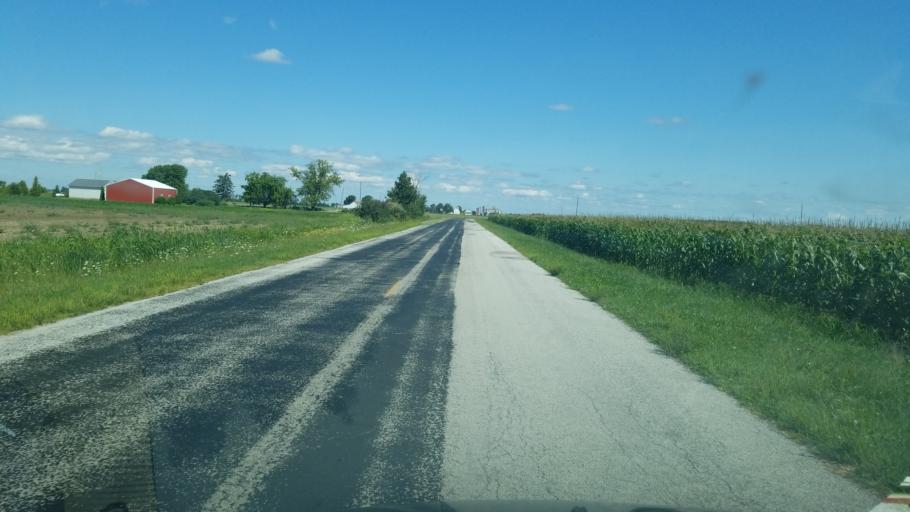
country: US
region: Ohio
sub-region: Henry County
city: Deshler
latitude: 41.2532
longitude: -83.8427
